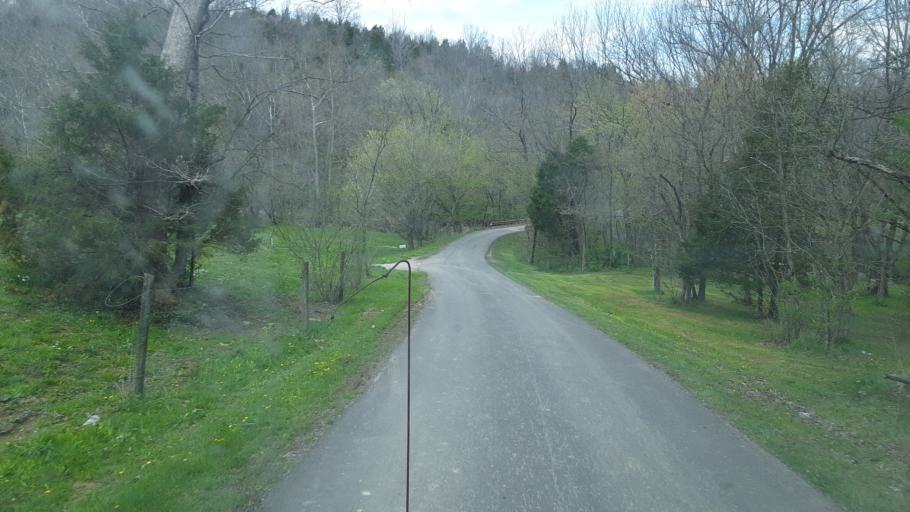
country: US
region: Kentucky
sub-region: Owen County
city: Owenton
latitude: 38.6739
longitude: -84.7978
